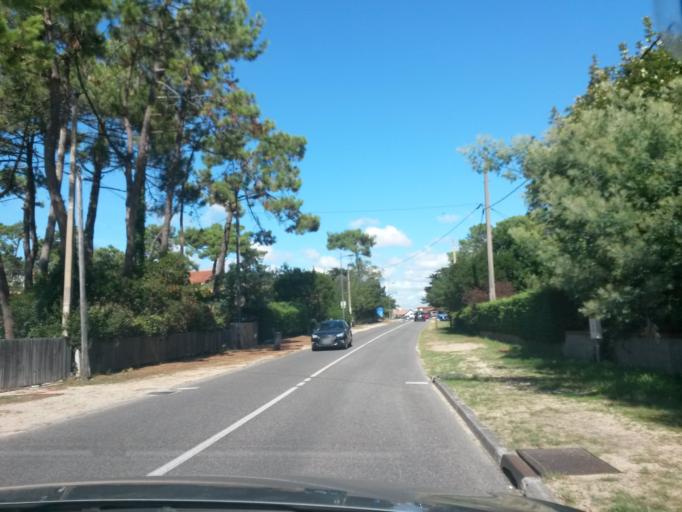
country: FR
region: Aquitaine
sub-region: Departement de la Gironde
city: Arcachon
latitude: 44.6968
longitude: -1.2319
